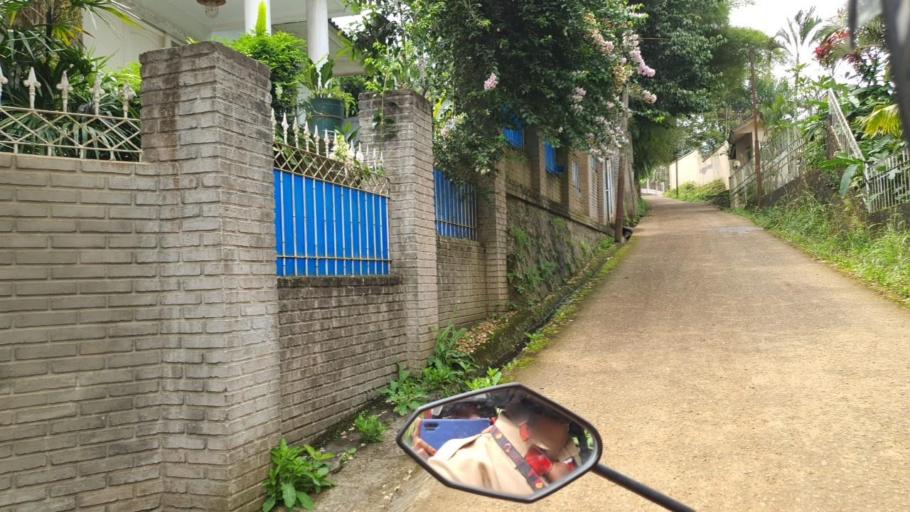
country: ID
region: West Java
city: Caringin
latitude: -6.6547
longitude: 106.8846
